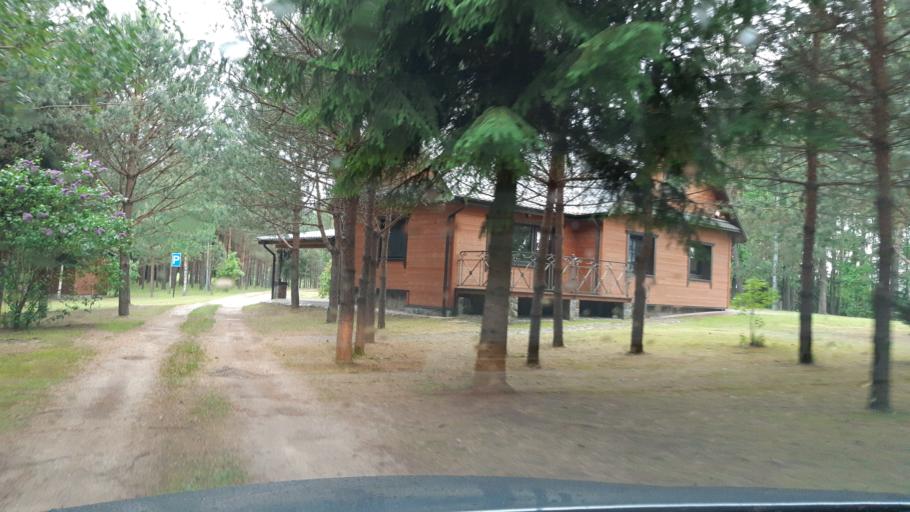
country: LT
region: Utenos apskritis
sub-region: Anyksciai
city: Anyksciai
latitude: 55.4466
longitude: 25.1926
